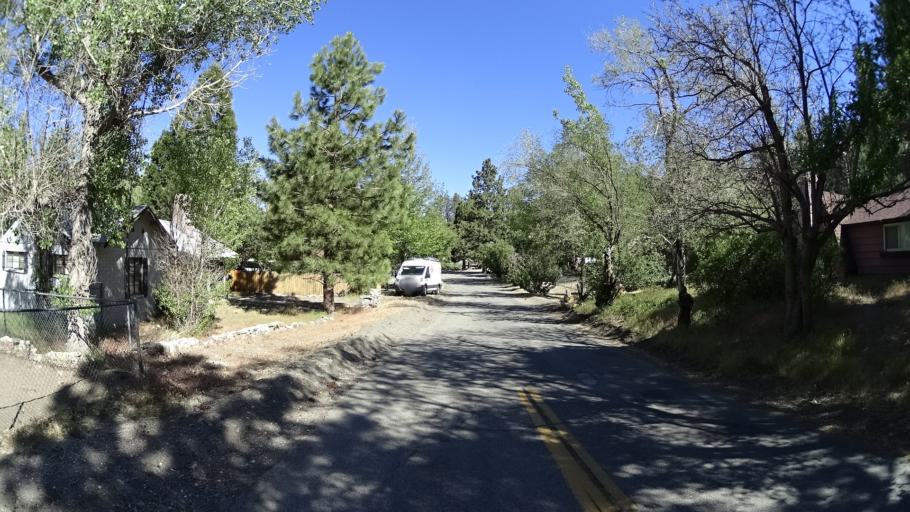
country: US
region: California
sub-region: San Bernardino County
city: Wrightwood
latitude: 34.3619
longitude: -117.6422
